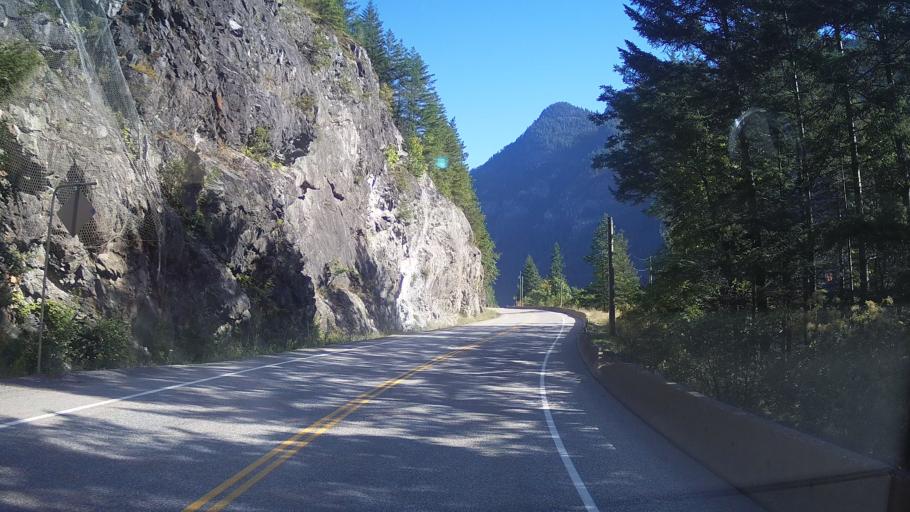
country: CA
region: British Columbia
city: Hope
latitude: 49.5721
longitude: -121.4038
